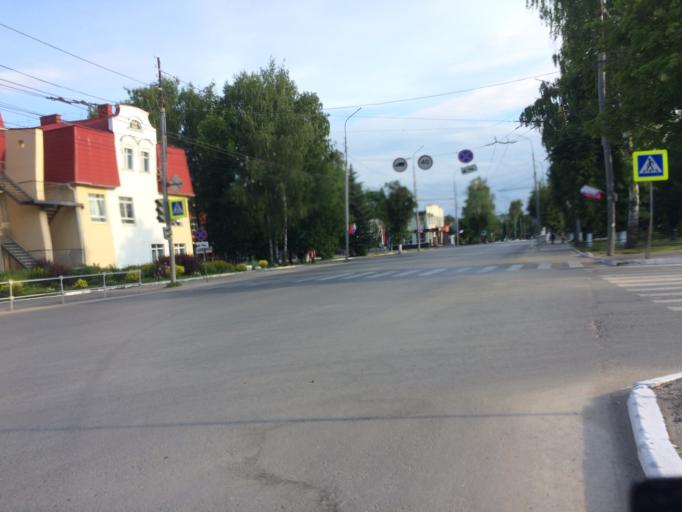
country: RU
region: Mariy-El
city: Medvedevo
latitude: 56.6325
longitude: 47.8040
